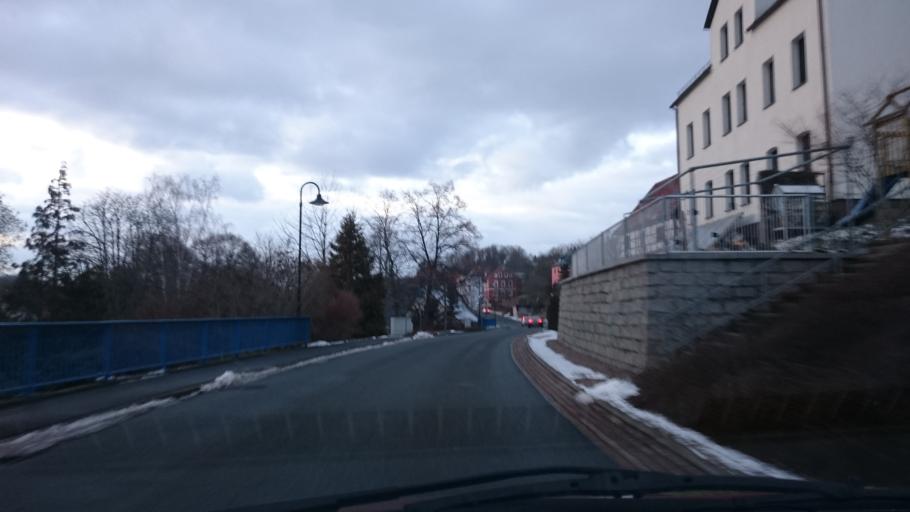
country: DE
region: Saxony
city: Reinsdorf
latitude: 50.7007
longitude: 12.5545
